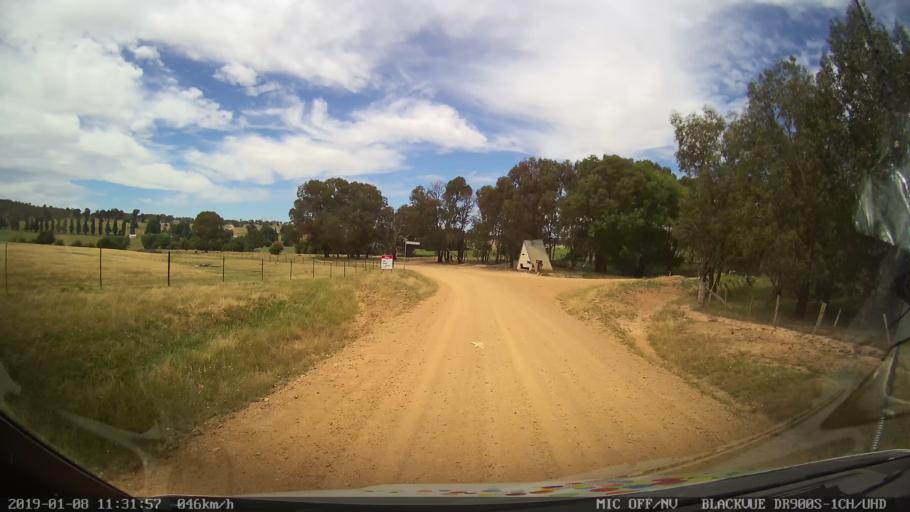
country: AU
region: New South Wales
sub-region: Guyra
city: Guyra
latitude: -30.3155
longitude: 151.5339
